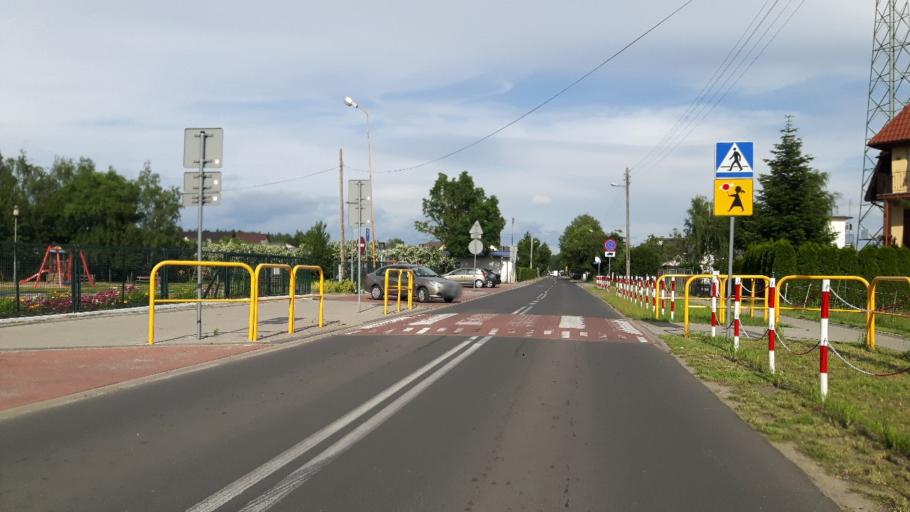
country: PL
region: West Pomeranian Voivodeship
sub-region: Powiat goleniowski
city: Goleniow
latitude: 53.4621
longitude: 14.7747
